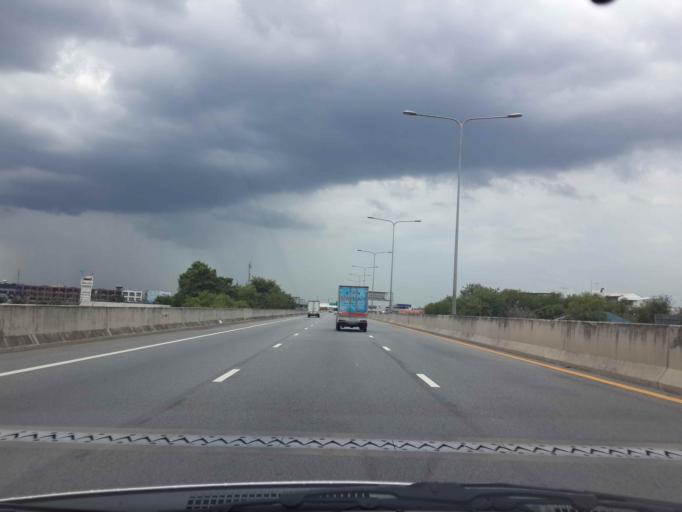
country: TH
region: Bangkok
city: Bang Khen
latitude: 13.8705
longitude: 100.6461
